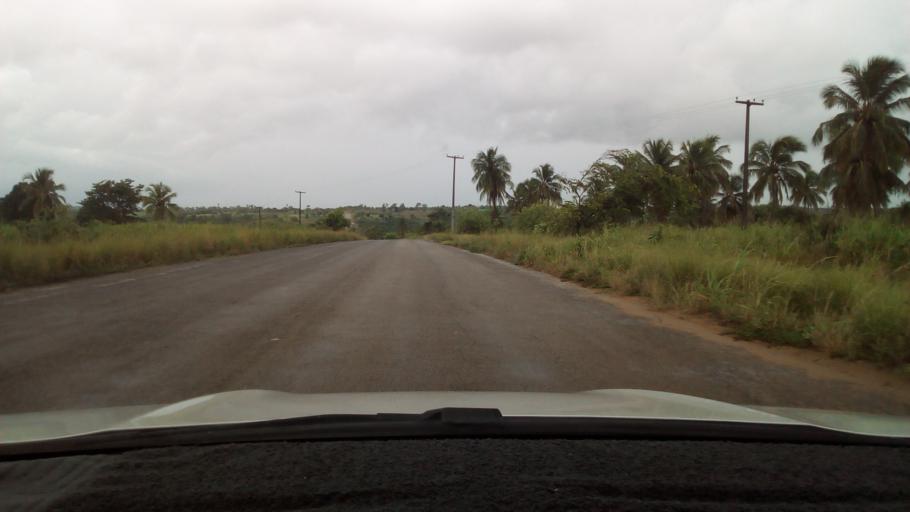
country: BR
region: Paraiba
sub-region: Pitimbu
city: Pitimbu
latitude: -7.4128
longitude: -34.8243
